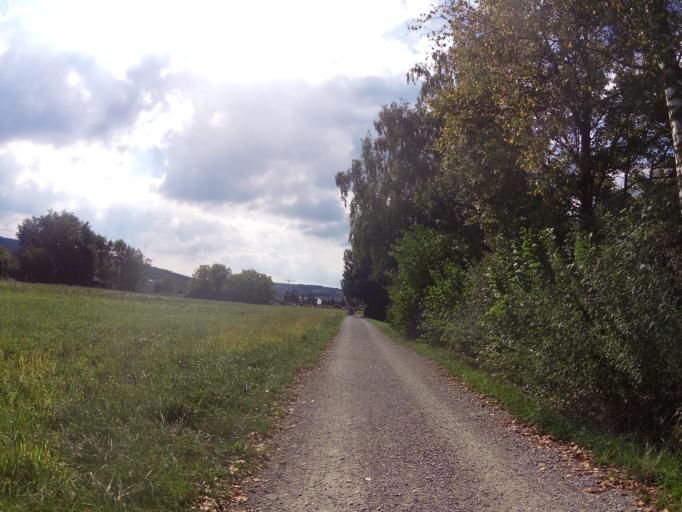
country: CH
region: Zurich
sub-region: Bezirk Dietikon
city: Schlieren / Engstingerquartier
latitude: 47.4075
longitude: 8.4423
